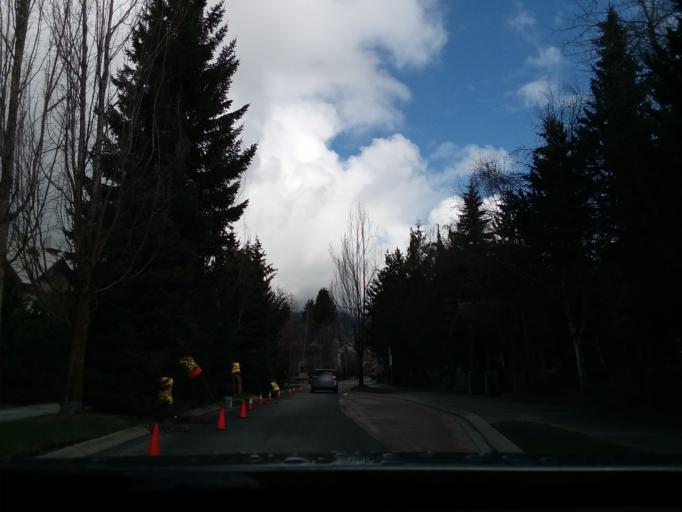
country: CA
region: British Columbia
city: Whistler
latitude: 50.1189
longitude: -122.9584
